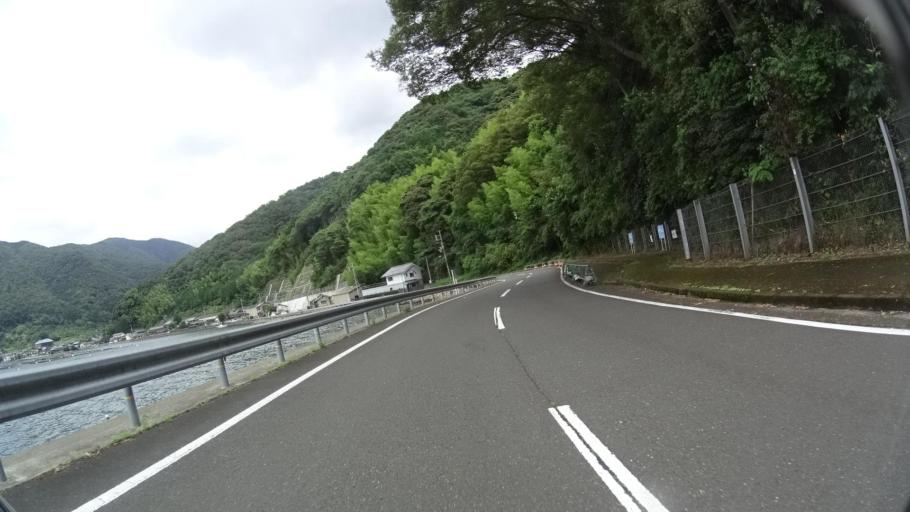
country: JP
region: Kyoto
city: Maizuru
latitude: 35.5216
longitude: 135.3452
